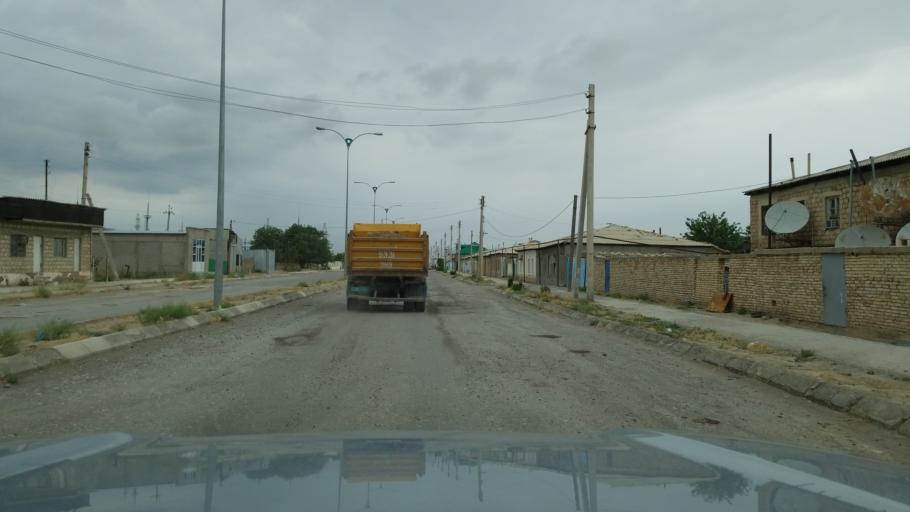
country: TM
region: Balkan
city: Serdar
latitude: 38.9712
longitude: 56.2590
